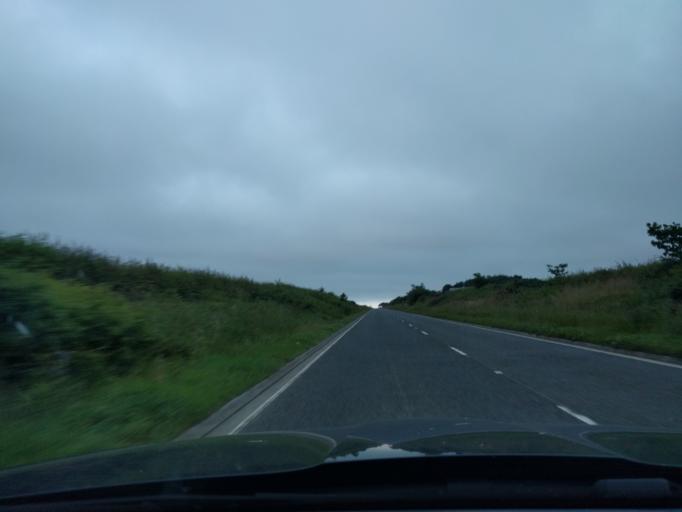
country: GB
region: England
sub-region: Northumberland
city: Felton
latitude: 55.2501
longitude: -1.6975
